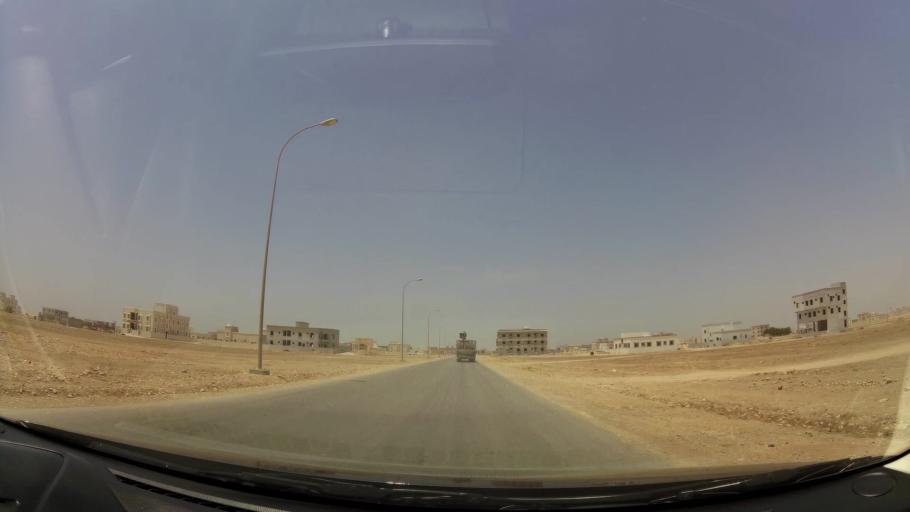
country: OM
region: Zufar
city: Salalah
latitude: 17.0947
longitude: 54.2106
